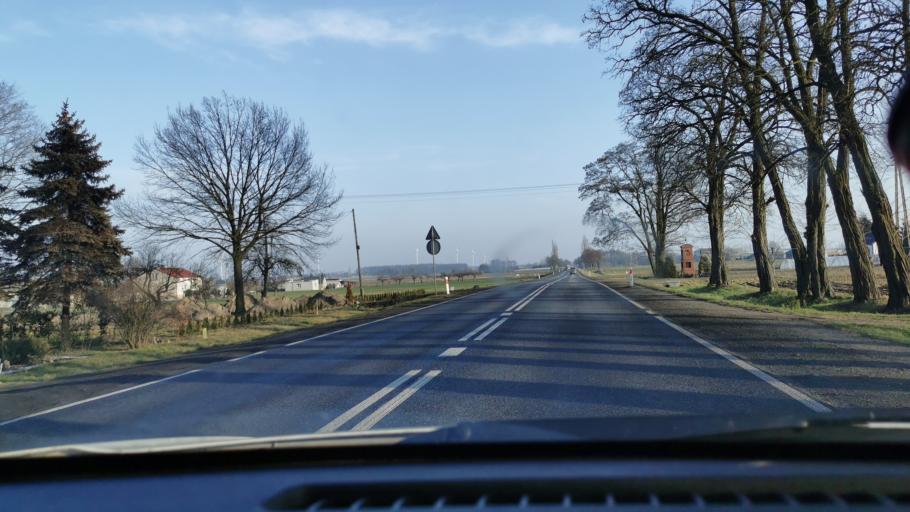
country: PL
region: Lodz Voivodeship
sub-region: Powiat sieradzki
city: Blaszki
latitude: 51.6439
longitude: 18.4826
